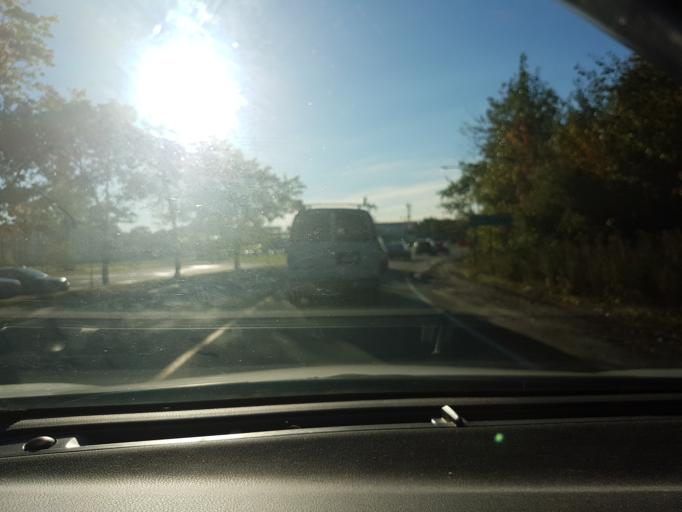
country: CA
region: Quebec
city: L'Ancienne-Lorette
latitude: 46.7965
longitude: -71.3162
